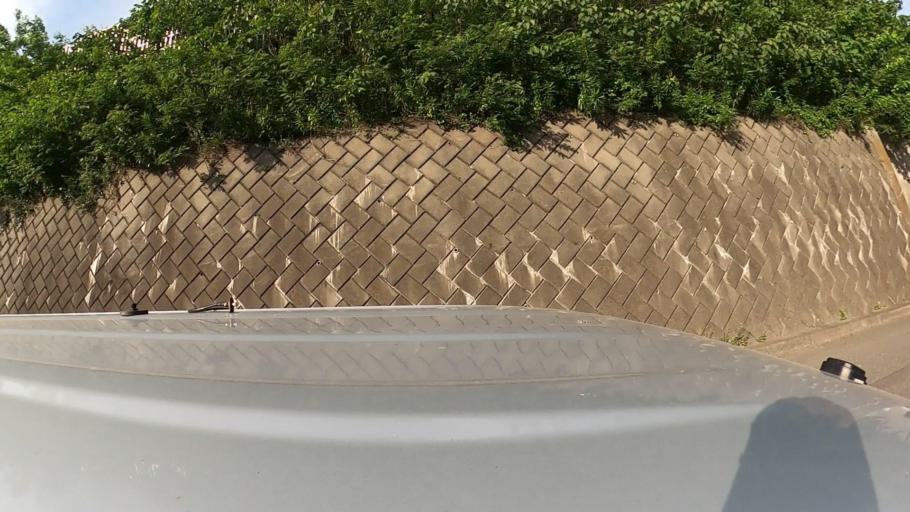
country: JP
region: Saitama
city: Asaka
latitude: 35.7804
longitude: 139.5634
